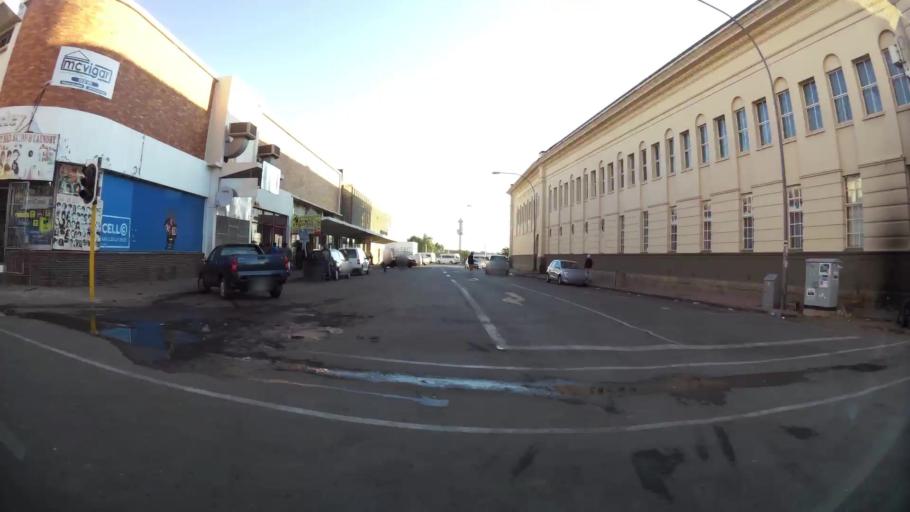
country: ZA
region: Northern Cape
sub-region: Frances Baard District Municipality
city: Kimberley
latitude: -28.7392
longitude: 24.7622
